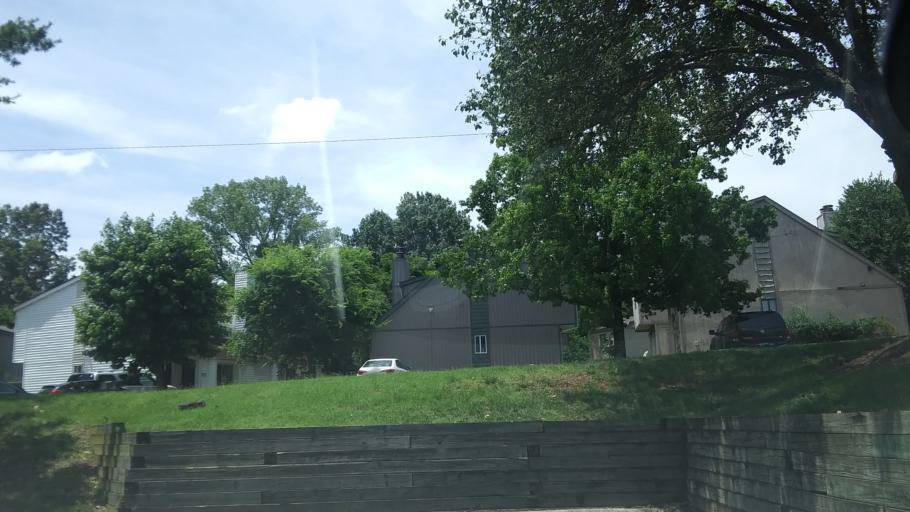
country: US
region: Tennessee
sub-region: Rutherford County
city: La Vergne
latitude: 36.0906
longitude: -86.6421
